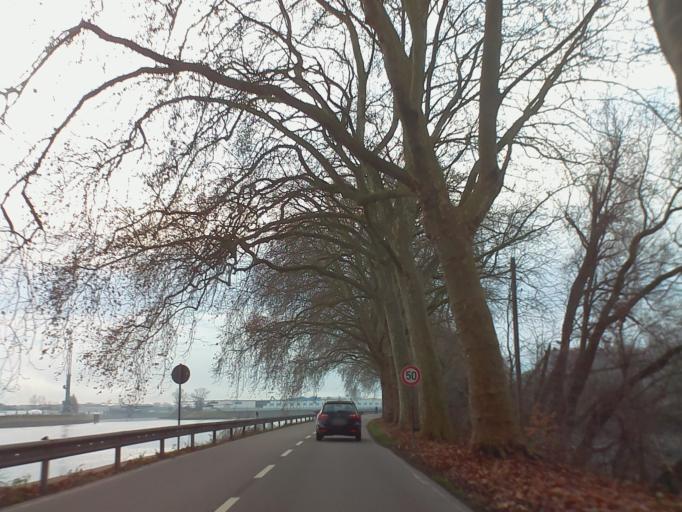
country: DE
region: Rheinland-Pfalz
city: Altrip
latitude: 49.4382
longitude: 8.5044
